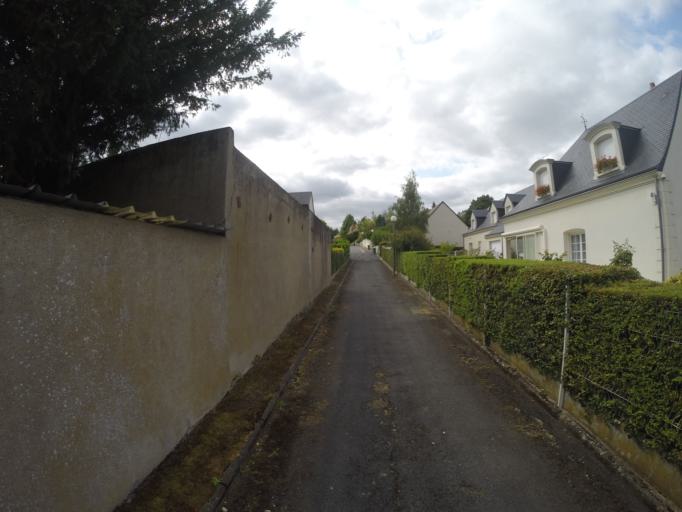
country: FR
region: Centre
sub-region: Departement d'Indre-et-Loire
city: Tours
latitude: 47.4088
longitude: 0.7079
